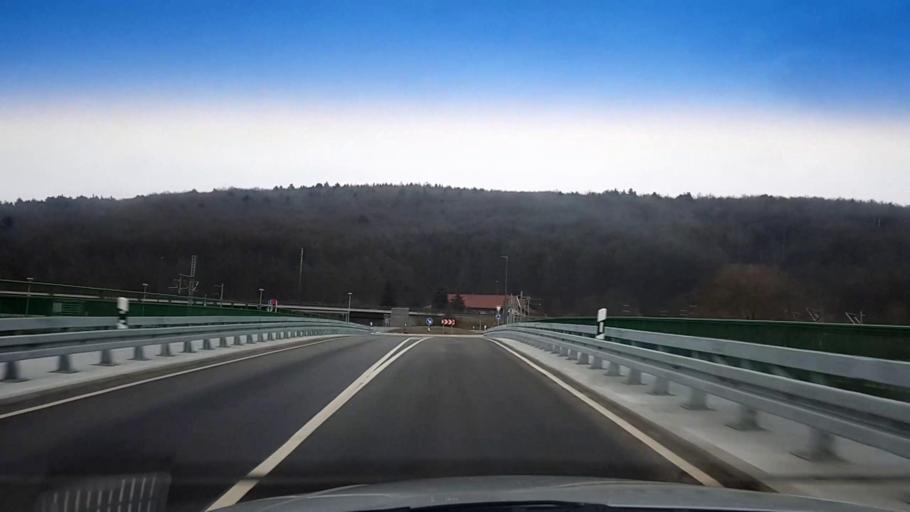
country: DE
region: Bavaria
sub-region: Upper Franconia
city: Zapfendorf
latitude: 50.0019
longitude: 10.9121
